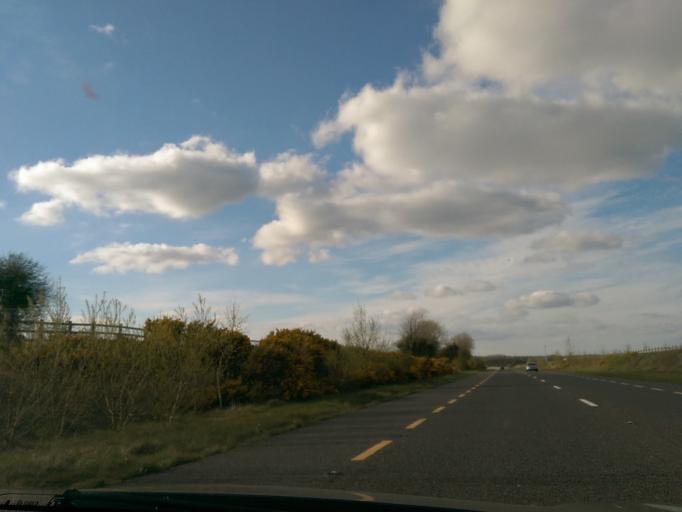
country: IE
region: Connaught
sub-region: County Galway
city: Loughrea
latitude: 53.2495
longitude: -8.5946
